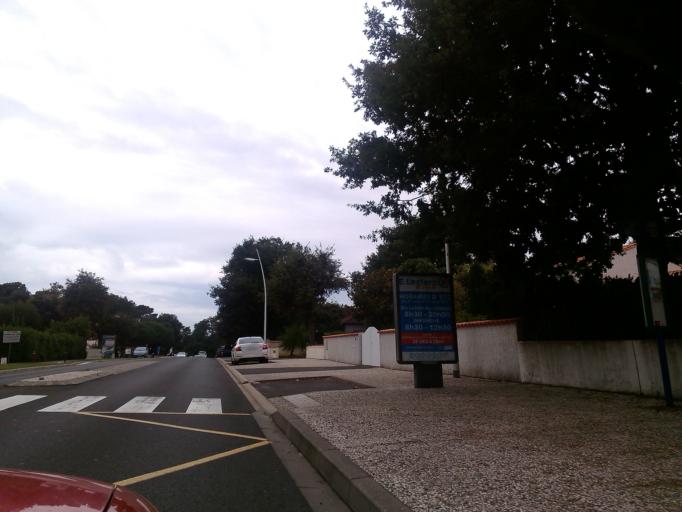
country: FR
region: Poitou-Charentes
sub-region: Departement de la Charente-Maritime
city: Vaux-sur-Mer
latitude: 45.6372
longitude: -1.0712
